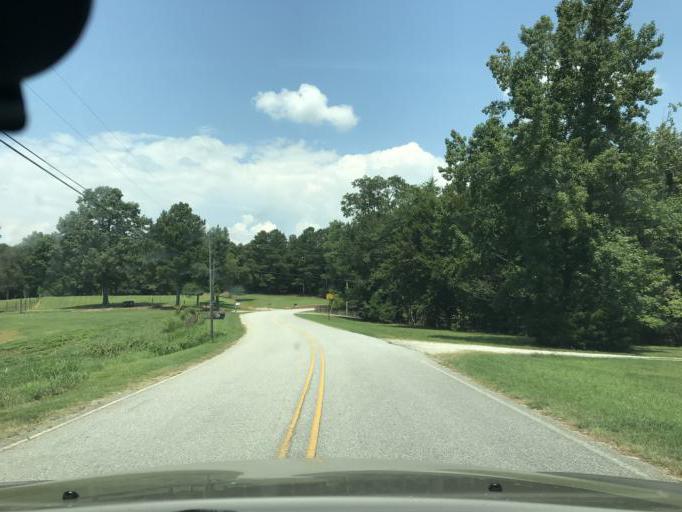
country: US
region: Georgia
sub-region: Dawson County
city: Dawsonville
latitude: 34.3473
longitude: -84.0877
